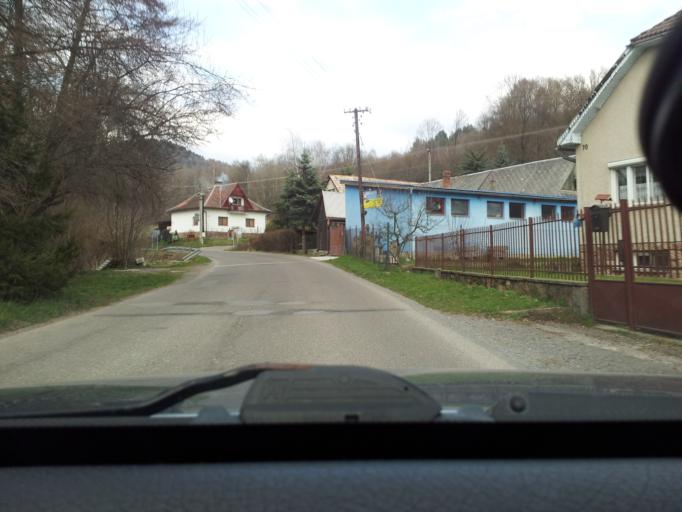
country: SK
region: Banskobystricky
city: Nova Bana
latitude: 48.4496
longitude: 18.6388
